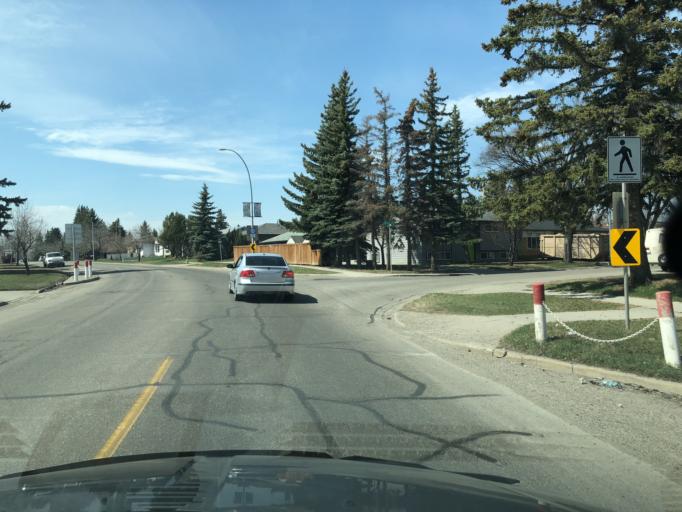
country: CA
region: Alberta
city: Calgary
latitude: 50.9721
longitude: -114.0530
